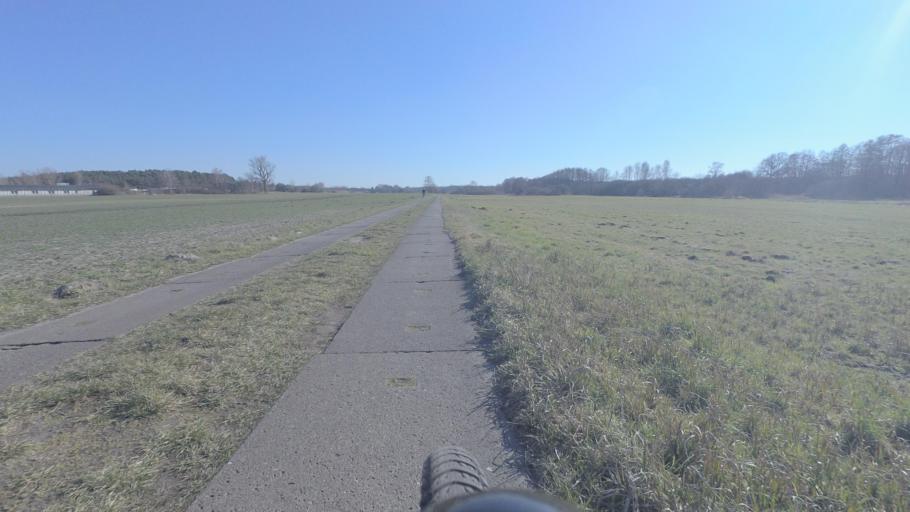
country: DE
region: Brandenburg
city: Rangsdorf
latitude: 52.2572
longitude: 13.4126
